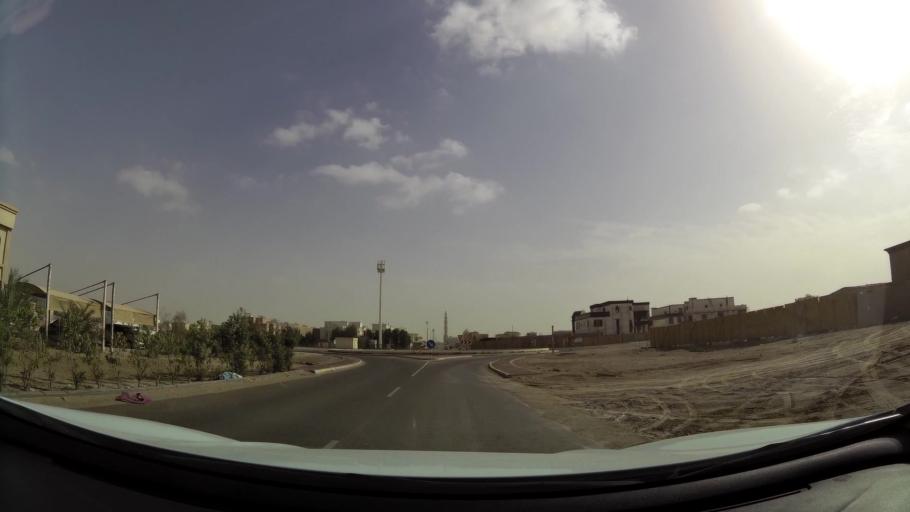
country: AE
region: Abu Dhabi
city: Abu Dhabi
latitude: 24.4336
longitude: 54.5918
